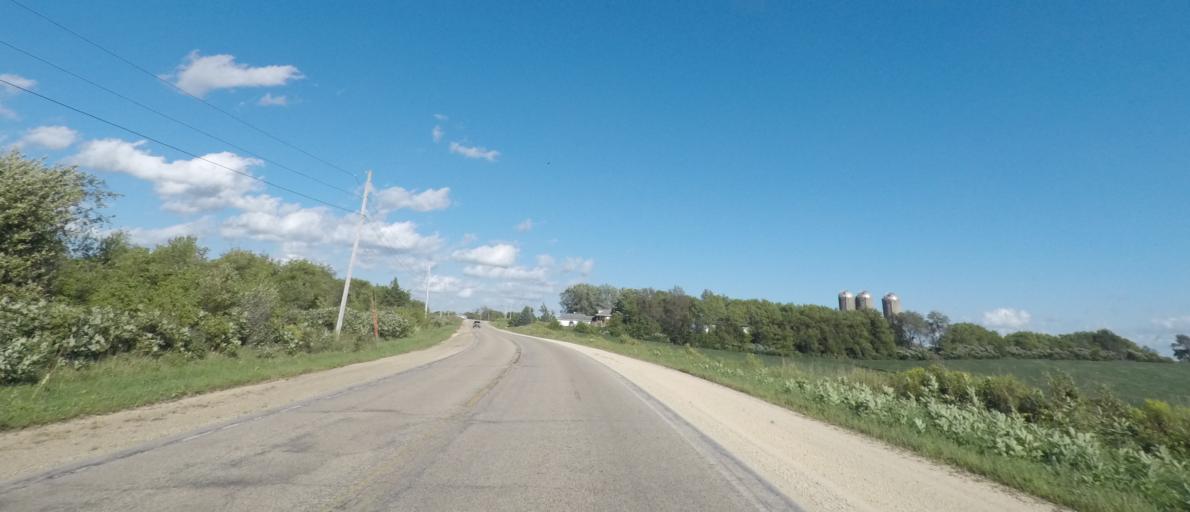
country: US
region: Wisconsin
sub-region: Iowa County
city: Dodgeville
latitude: 42.9794
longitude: -90.0667
